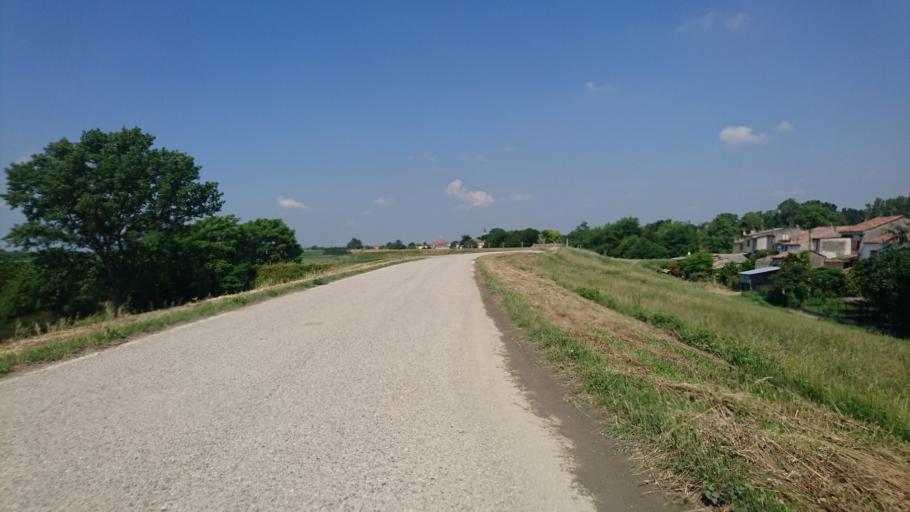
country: IT
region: Lombardy
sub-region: Provincia di Mantova
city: Sustinente
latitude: 45.0660
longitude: 11.0285
